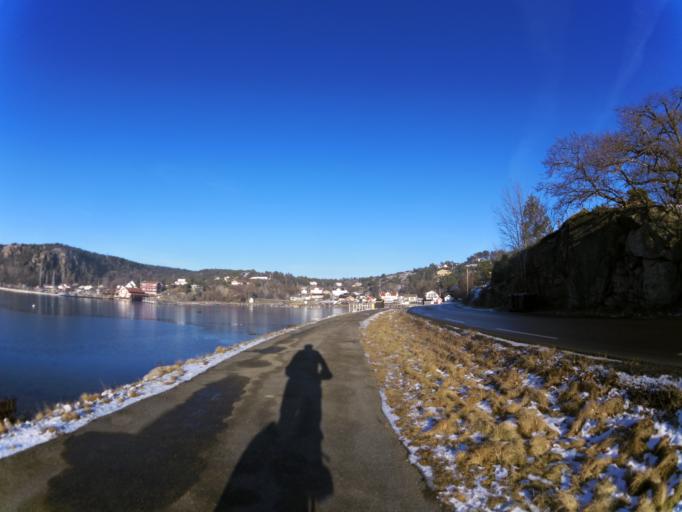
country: NO
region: Ostfold
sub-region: Fredrikstad
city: Lervik
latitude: 59.2051
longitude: 10.8031
